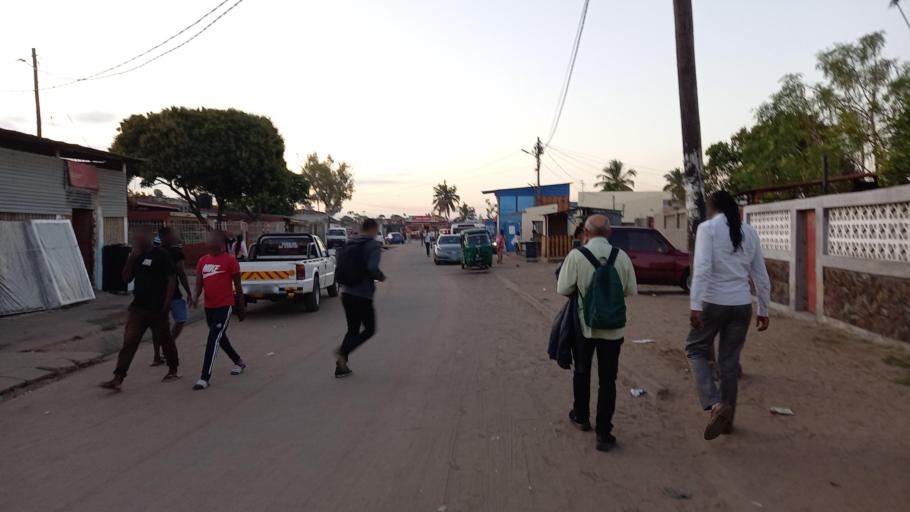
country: MZ
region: Maputo City
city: Maputo
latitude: -25.9515
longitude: 32.5714
